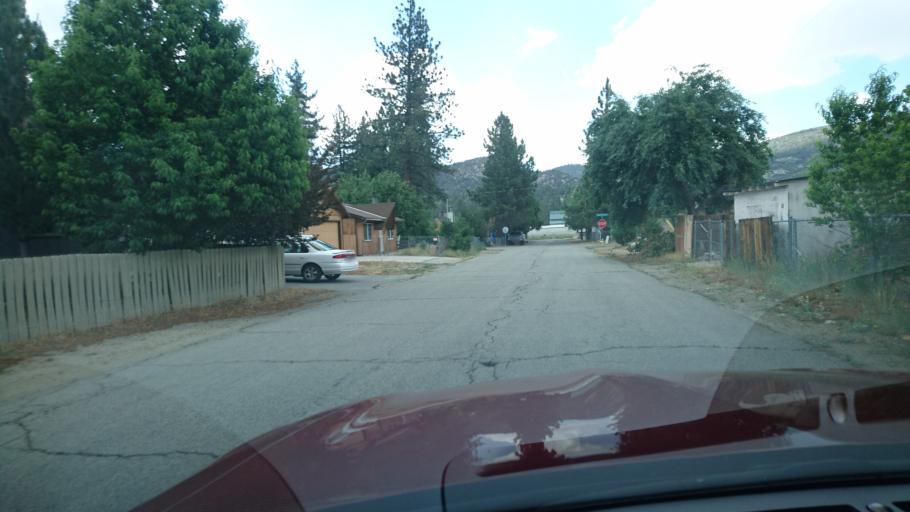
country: US
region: California
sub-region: San Bernardino County
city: Big Bear City
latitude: 34.2612
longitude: -116.8569
